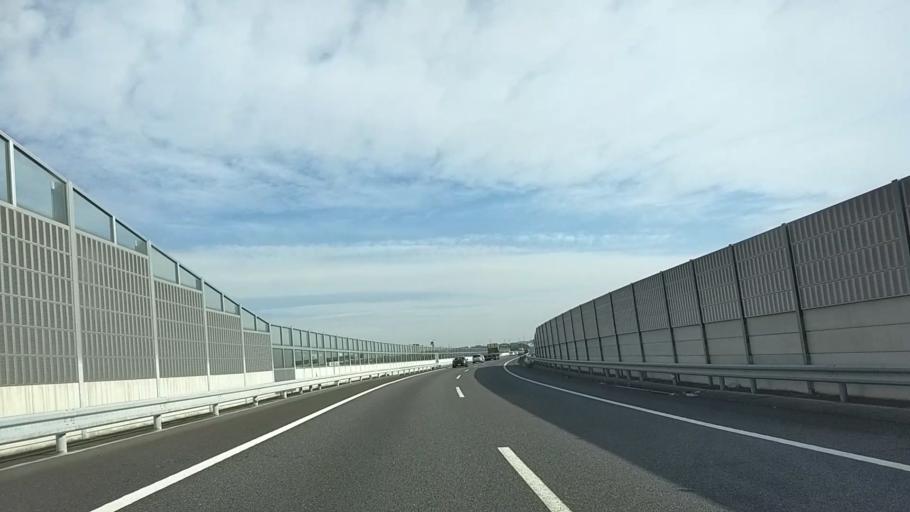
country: JP
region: Kanagawa
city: Zama
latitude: 35.5004
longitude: 139.3656
